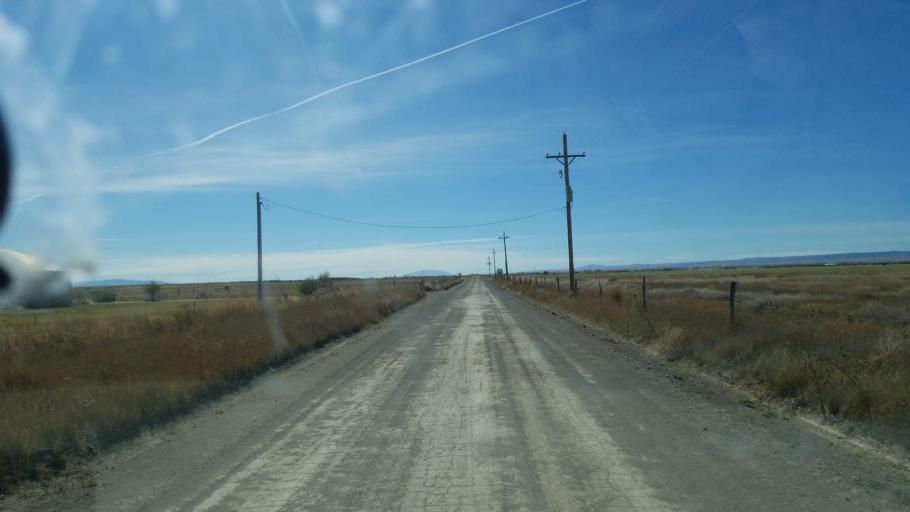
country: US
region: Colorado
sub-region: Rio Grande County
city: Monte Vista
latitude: 37.5384
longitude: -106.0758
